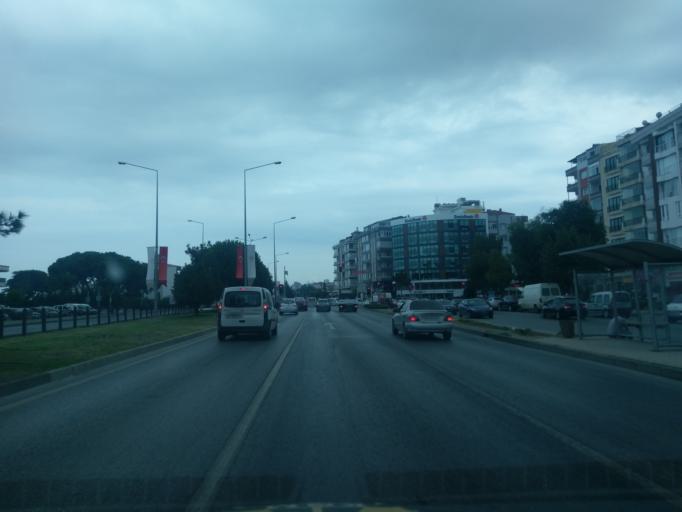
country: TR
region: Samsun
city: Samsun
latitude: 41.3331
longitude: 36.2829
